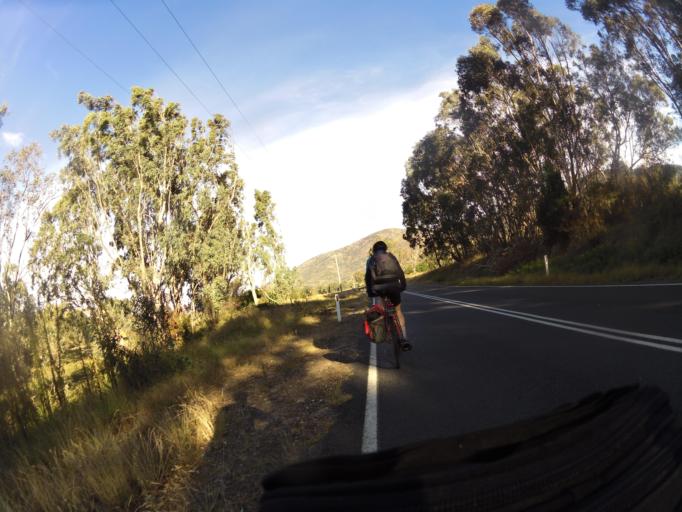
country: AU
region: New South Wales
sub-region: Greater Hume Shire
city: Holbrook
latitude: -35.9803
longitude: 147.8170
